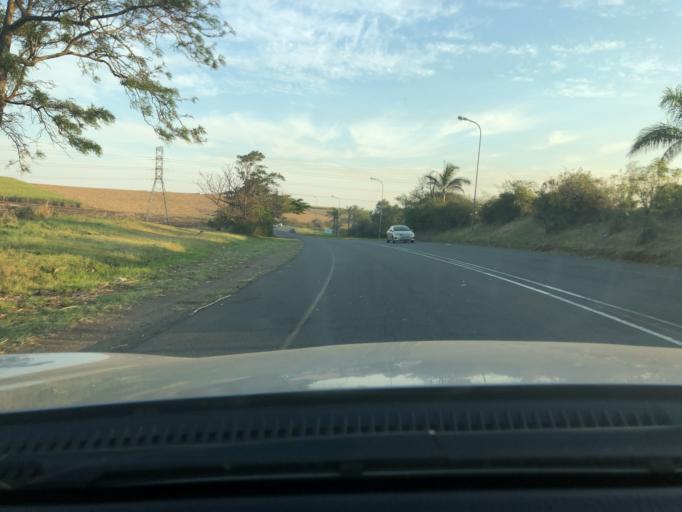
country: ZA
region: KwaZulu-Natal
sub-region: iLembe District Municipality
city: Ballitoville
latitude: -29.5864
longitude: 31.1010
